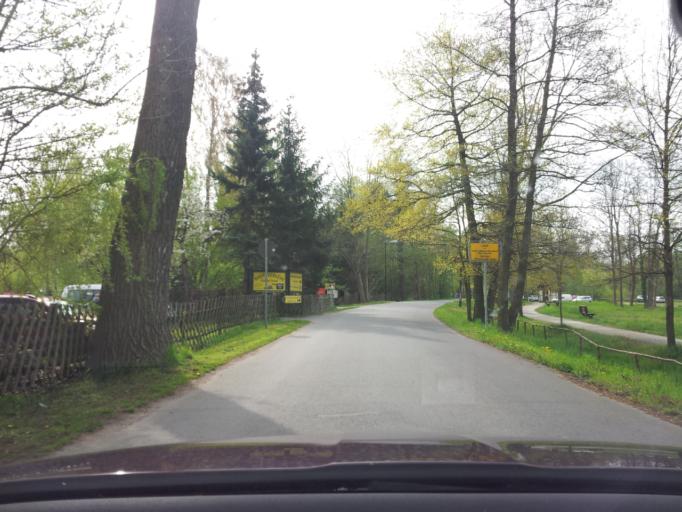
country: DE
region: Brandenburg
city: Lubbenau
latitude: 51.8675
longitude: 13.9882
